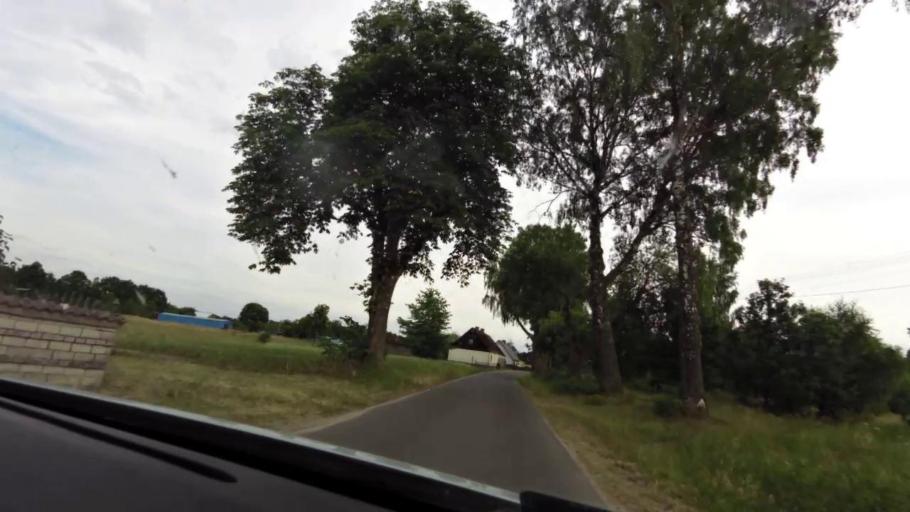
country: PL
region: Pomeranian Voivodeship
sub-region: Powiat bytowski
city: Trzebielino
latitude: 54.2611
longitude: 17.0103
